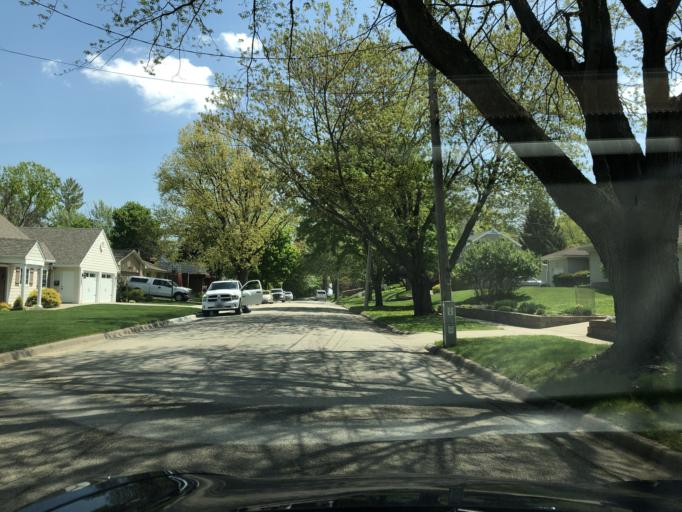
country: US
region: Iowa
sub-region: Dubuque County
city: Dubuque
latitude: 42.4797
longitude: -90.6631
